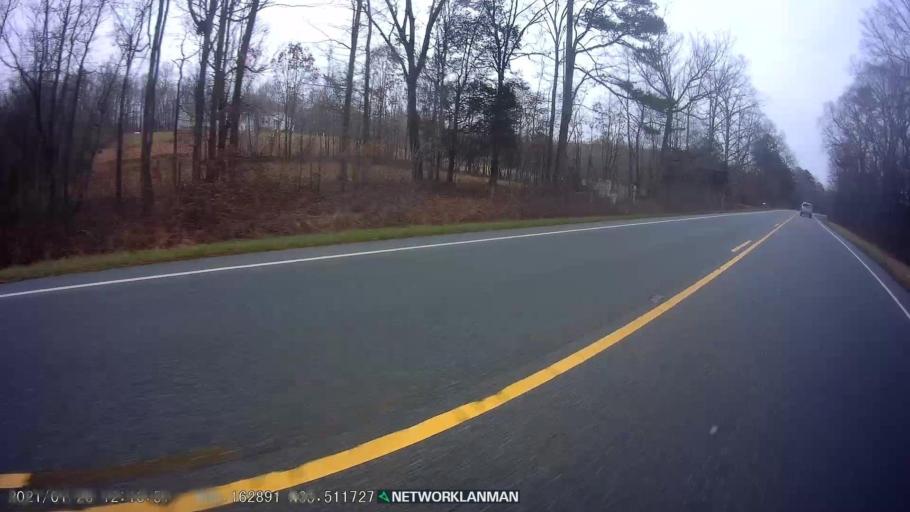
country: US
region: North Carolina
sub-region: Stanly County
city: Badin
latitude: 35.5118
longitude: -80.1624
